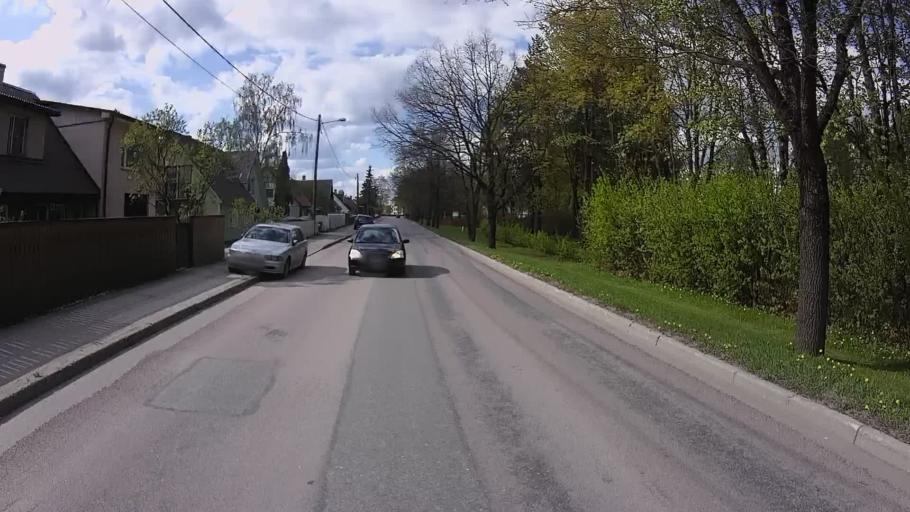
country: EE
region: Tartu
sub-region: Tartu linn
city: Tartu
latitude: 58.3989
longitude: 26.7314
